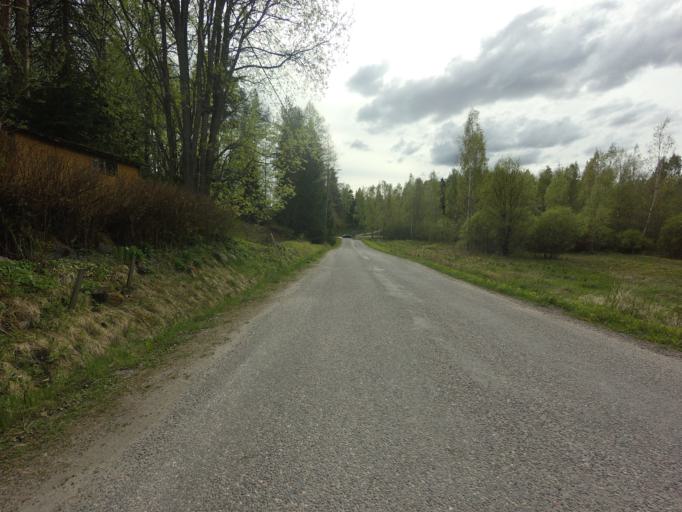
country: FI
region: Uusimaa
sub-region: Helsinki
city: Kauniainen
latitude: 60.1857
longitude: 24.7198
